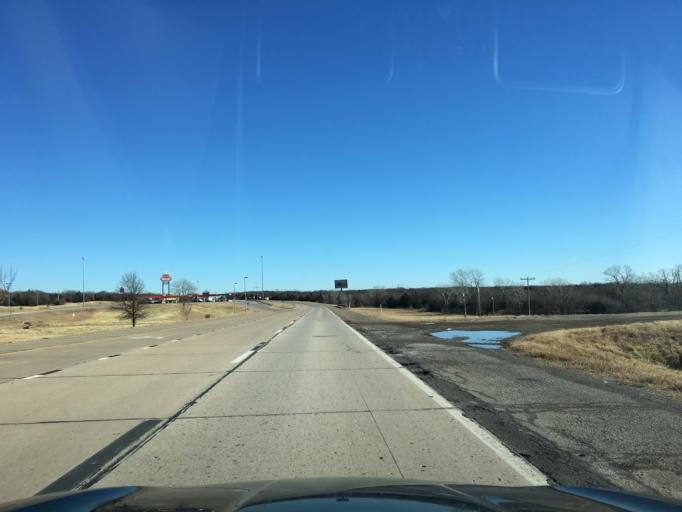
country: US
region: Oklahoma
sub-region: Pawnee County
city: Pawnee
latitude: 36.2246
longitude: -96.8016
